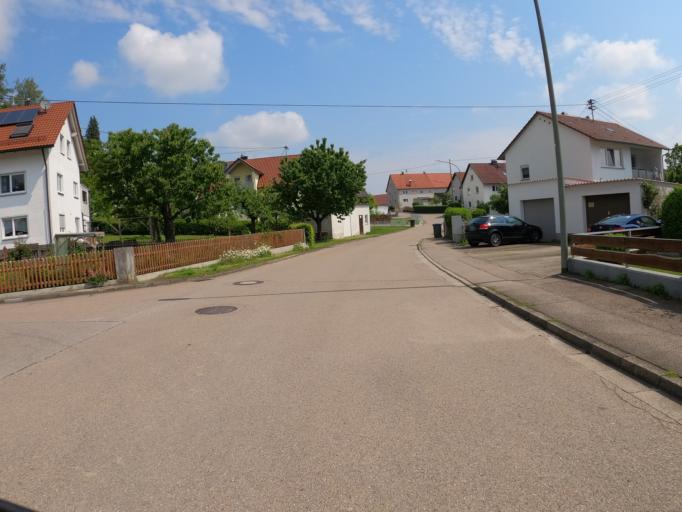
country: DE
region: Bavaria
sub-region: Swabia
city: Holzheim
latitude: 48.3763
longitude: 10.0929
